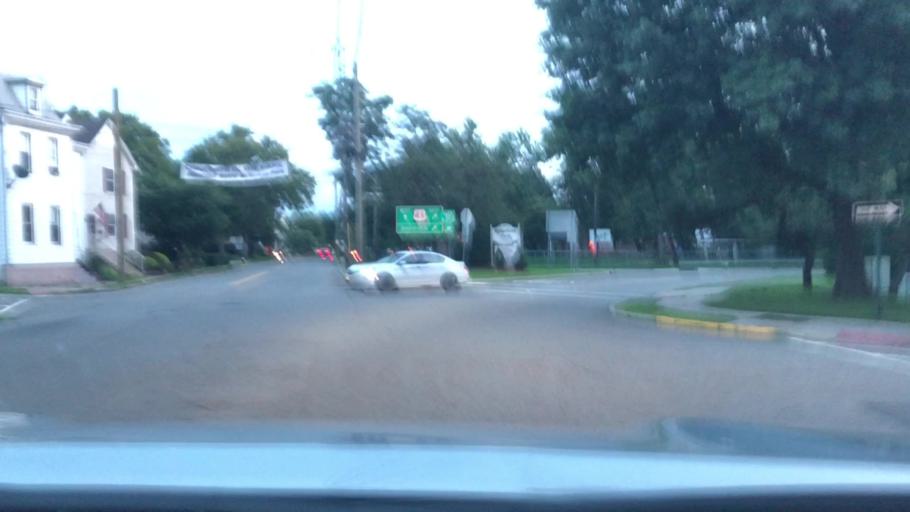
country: US
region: New Jersey
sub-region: Bergen County
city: Ridgefield Park
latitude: 40.8527
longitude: -74.0259
